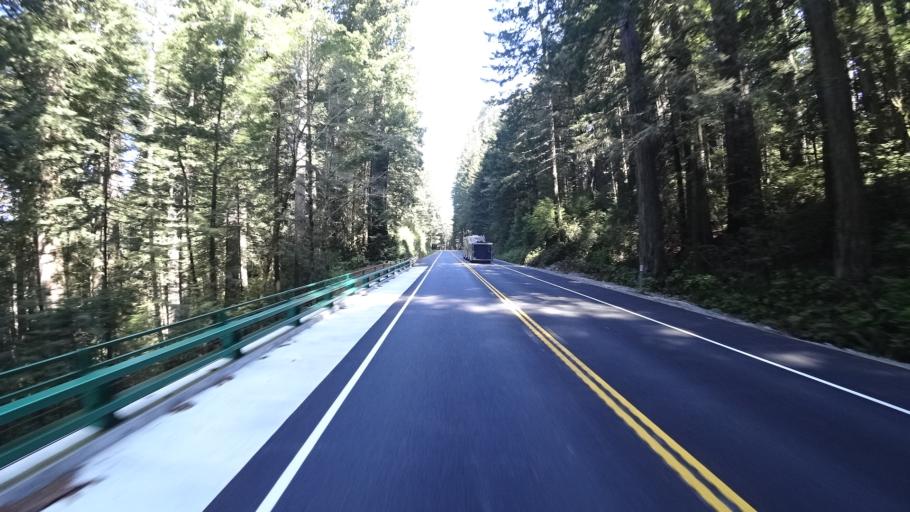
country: US
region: California
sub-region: Del Norte County
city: Bertsch-Oceanview
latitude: 41.6690
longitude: -124.1132
